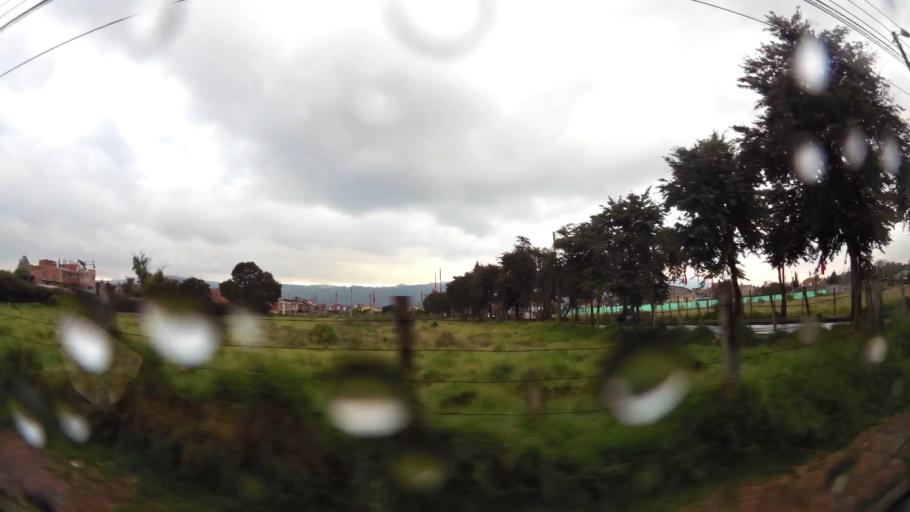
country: CO
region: Cundinamarca
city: Chia
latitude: 4.8676
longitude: -74.0578
